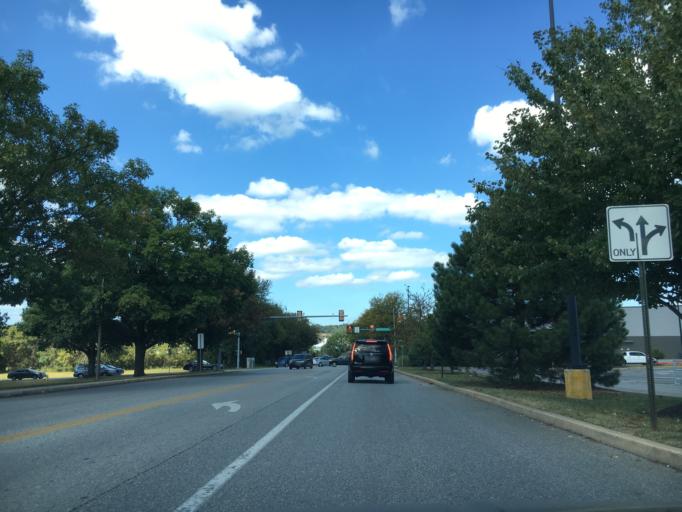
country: US
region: Pennsylvania
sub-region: York County
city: East York
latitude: 39.9791
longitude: -76.6748
